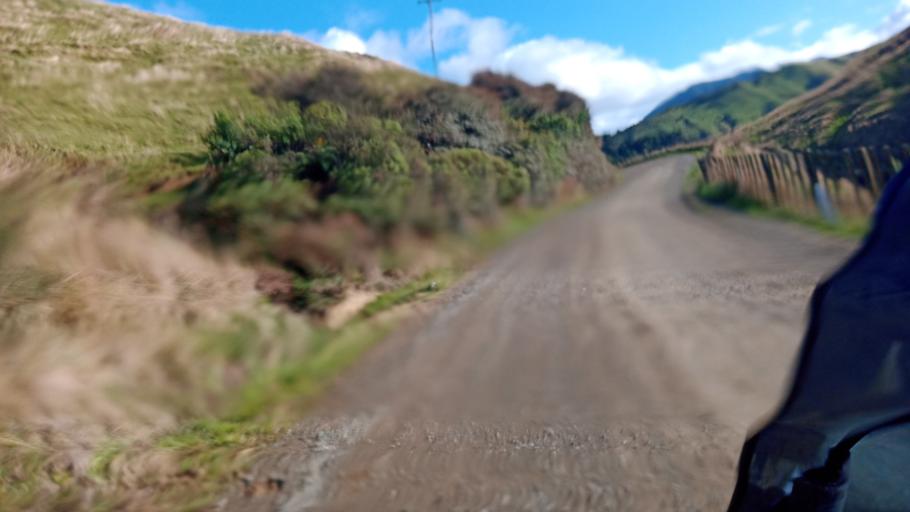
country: NZ
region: Bay of Plenty
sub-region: Opotiki District
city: Opotiki
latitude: -38.4678
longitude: 177.4292
